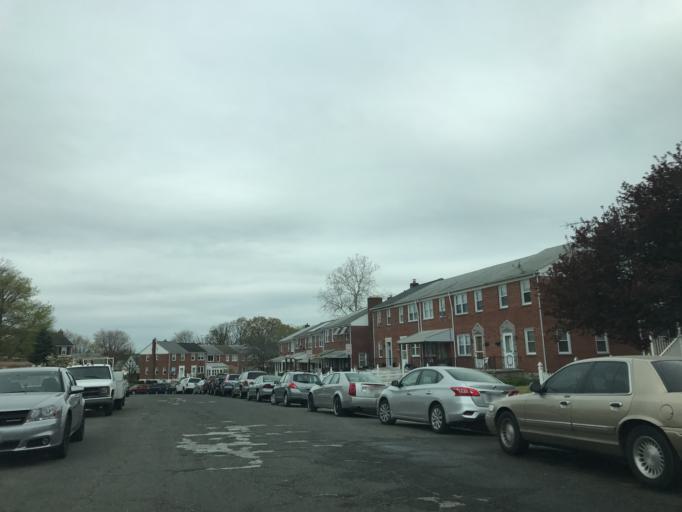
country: US
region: Maryland
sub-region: Baltimore County
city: Essex
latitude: 39.3091
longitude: -76.4831
